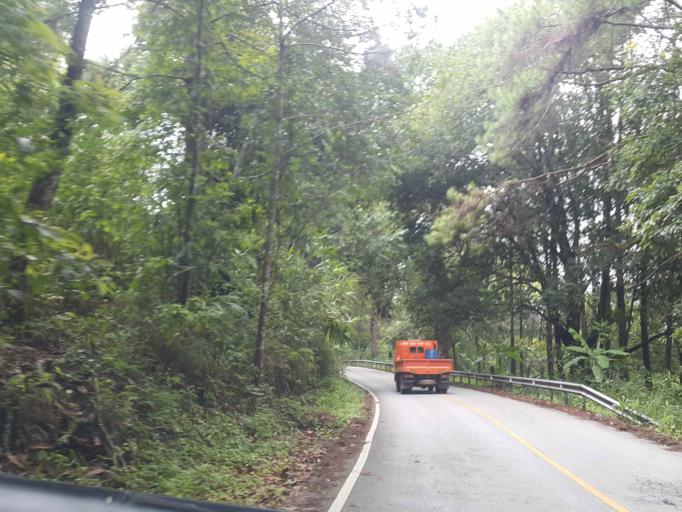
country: TH
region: Chiang Mai
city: Mae Chaem
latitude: 18.5175
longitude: 98.4634
